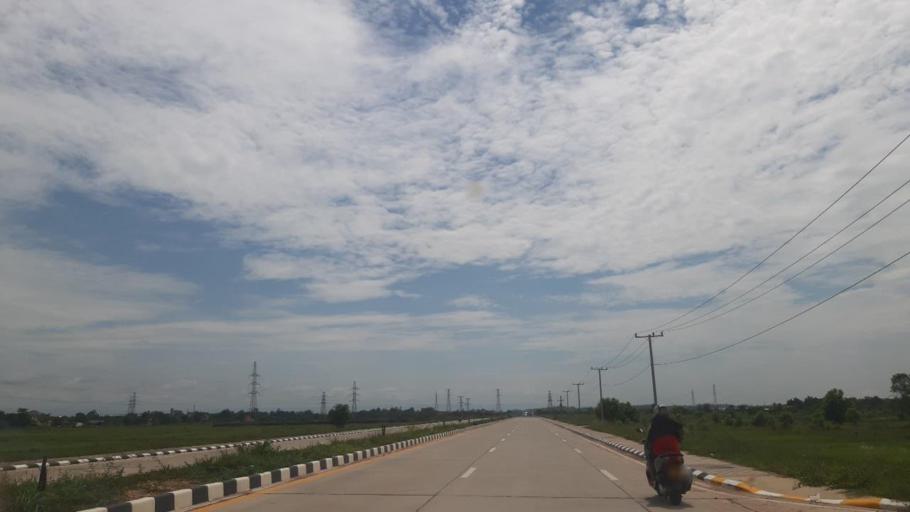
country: LA
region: Vientiane
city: Vientiane
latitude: 18.0193
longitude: 102.5927
